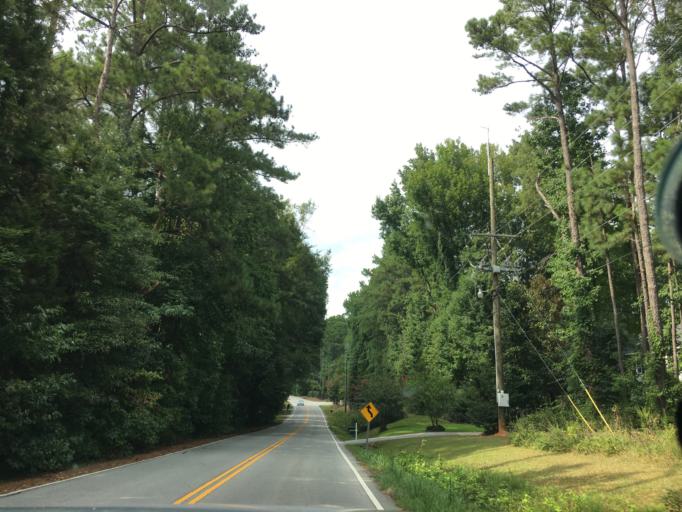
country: US
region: South Carolina
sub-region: Lexington County
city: Irmo
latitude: 34.0684
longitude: -81.1932
